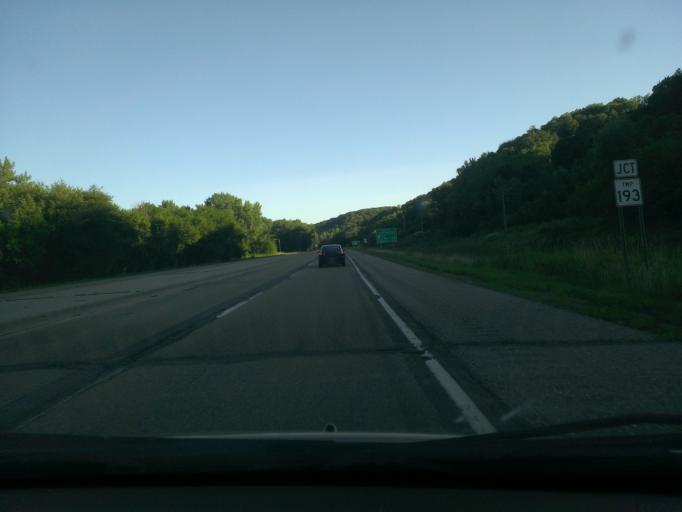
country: US
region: Minnesota
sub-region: Nicollet County
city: North Mankato
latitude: 44.2230
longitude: -94.0275
